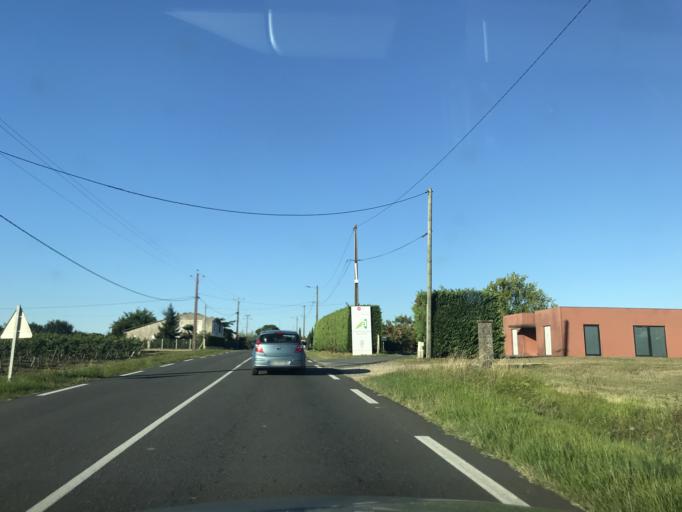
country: FR
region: Aquitaine
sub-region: Departement de la Gironde
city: Saint-Macaire
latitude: 44.5884
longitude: -0.2105
